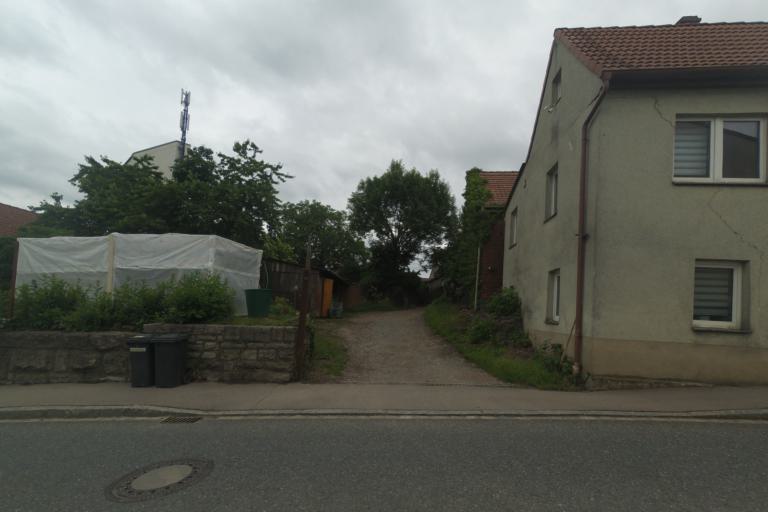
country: DE
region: Bavaria
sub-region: Regierungsbezirk Mittelfranken
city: Uffenheim
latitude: 49.5444
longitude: 10.2334
